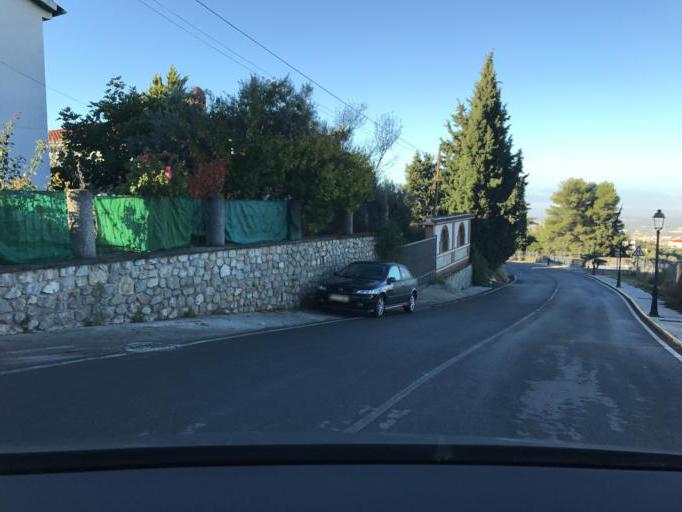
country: ES
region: Andalusia
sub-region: Provincia de Granada
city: Viznar
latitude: 37.2296
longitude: -3.5564
